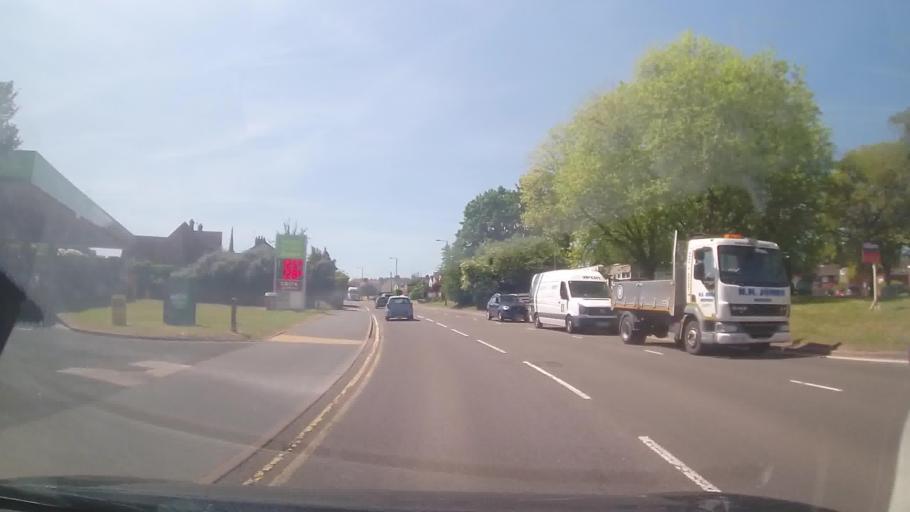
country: GB
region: England
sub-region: Herefordshire
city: Hereford
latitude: 52.0476
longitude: -2.7197
